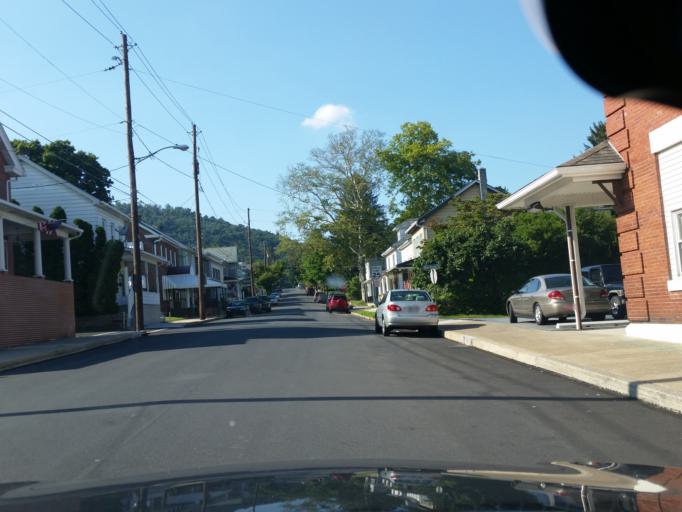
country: US
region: Pennsylvania
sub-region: Perry County
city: Marysville
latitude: 40.3444
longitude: -76.9314
